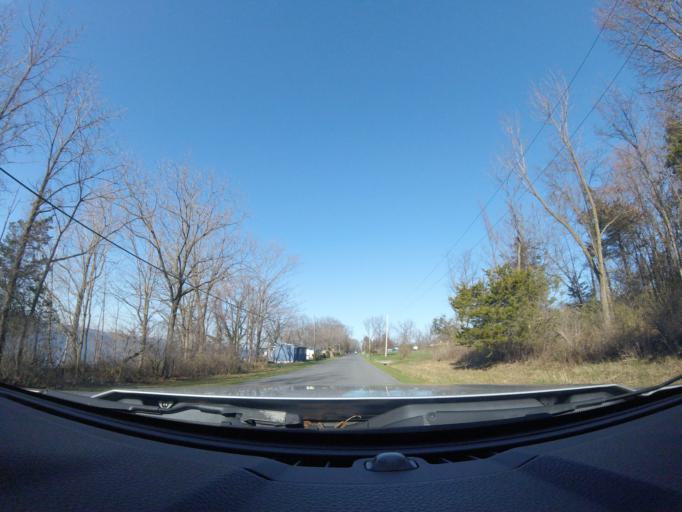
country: US
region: New York
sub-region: Cayuga County
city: Union Springs
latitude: 42.7238
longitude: -76.7091
